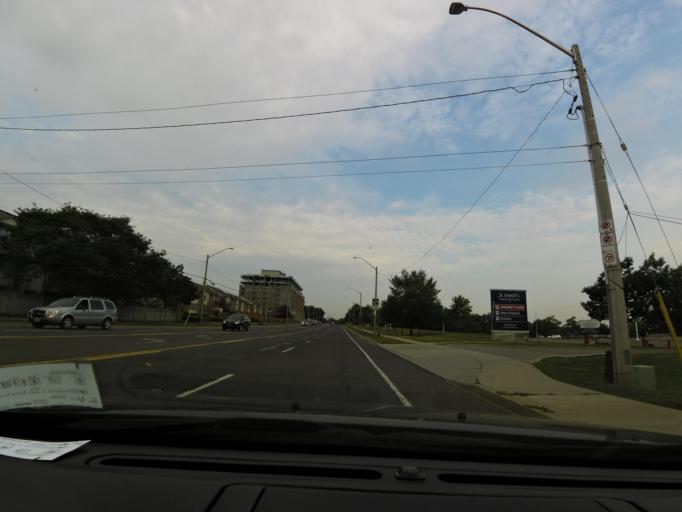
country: CA
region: Ontario
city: Hamilton
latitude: 43.2203
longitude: -79.7733
